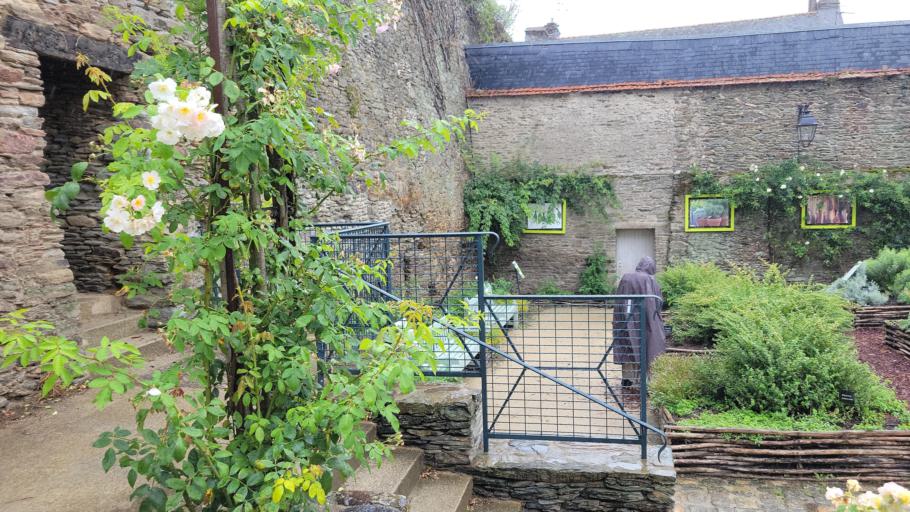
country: FR
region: Brittany
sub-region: Departement du Morbihan
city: Josselin
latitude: 47.9538
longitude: -2.5486
